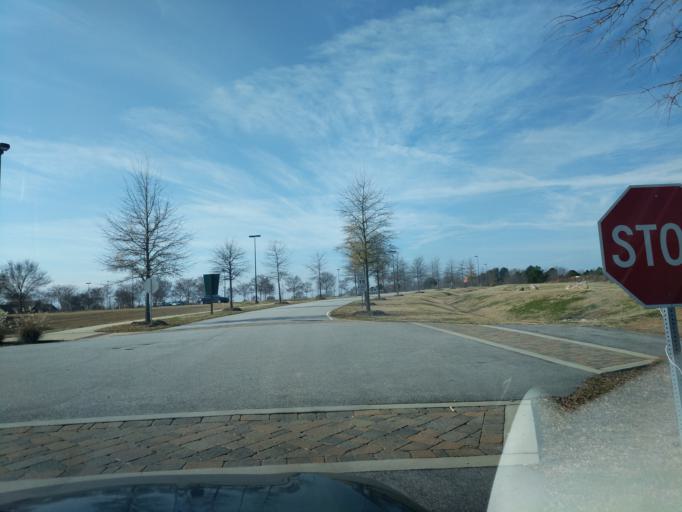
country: US
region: South Carolina
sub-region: Spartanburg County
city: Wellford
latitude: 34.8732
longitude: -82.1000
